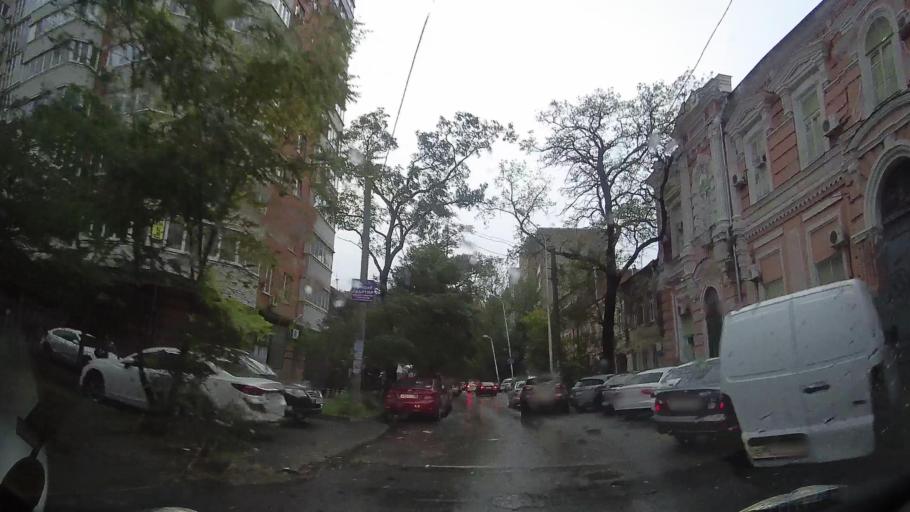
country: RU
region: Rostov
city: Rostov-na-Donu
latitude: 47.2285
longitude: 39.7034
